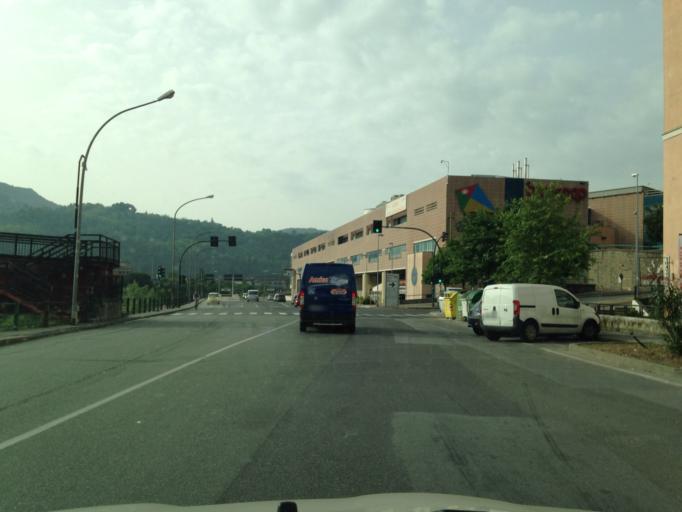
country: IT
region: Liguria
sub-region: Provincia di Genova
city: Manesseno
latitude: 44.4744
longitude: 8.8993
